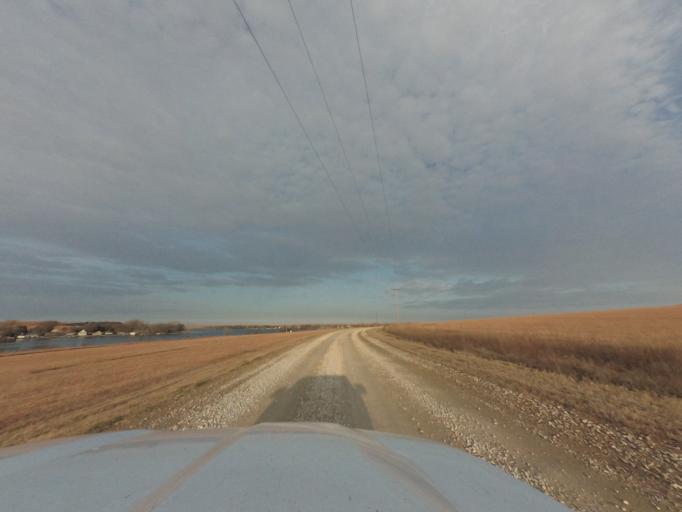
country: US
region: Kansas
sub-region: Morris County
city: Council Grove
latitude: 38.5195
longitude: -96.4107
